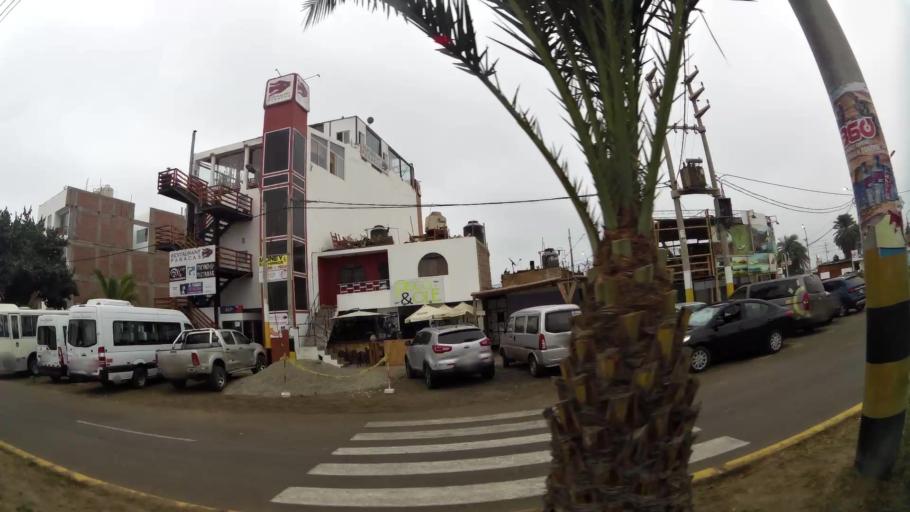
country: PE
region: Ica
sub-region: Provincia de Pisco
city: Paracas
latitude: -13.8334
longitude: -76.2479
